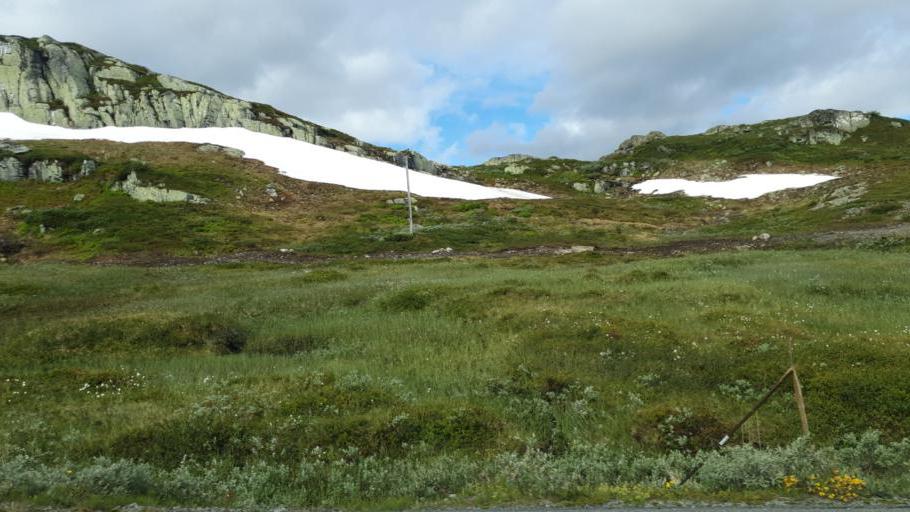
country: NO
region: Oppland
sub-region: Vestre Slidre
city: Slidre
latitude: 61.3115
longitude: 8.8076
